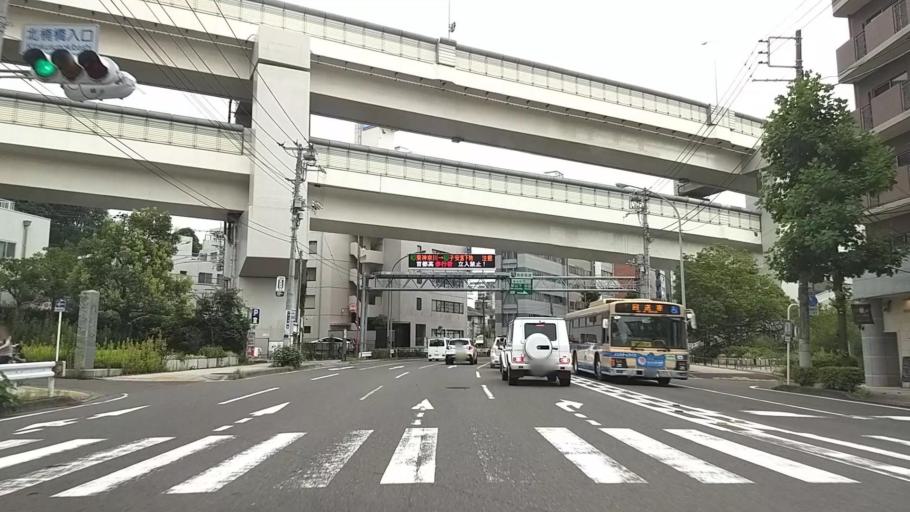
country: JP
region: Kanagawa
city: Yokohama
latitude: 35.4686
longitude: 139.6148
